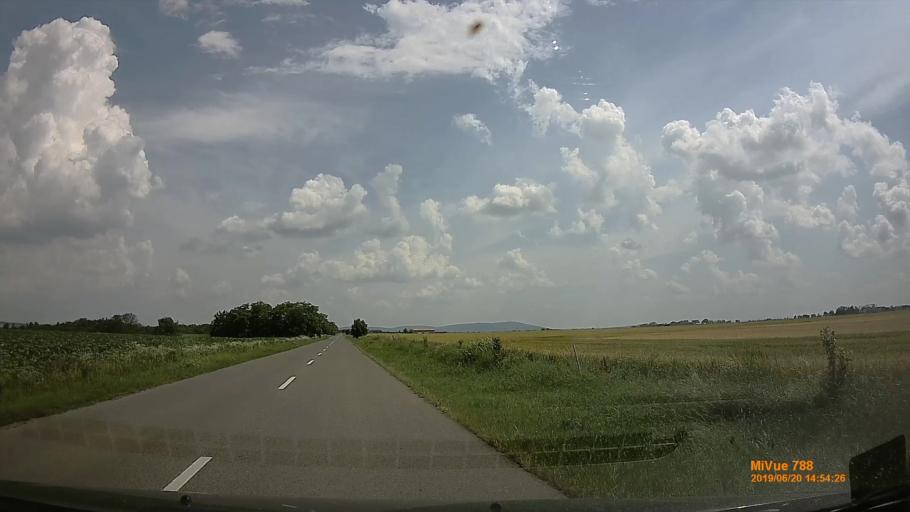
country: HU
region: Baranya
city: Kozarmisleny
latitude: 45.9996
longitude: 18.2422
